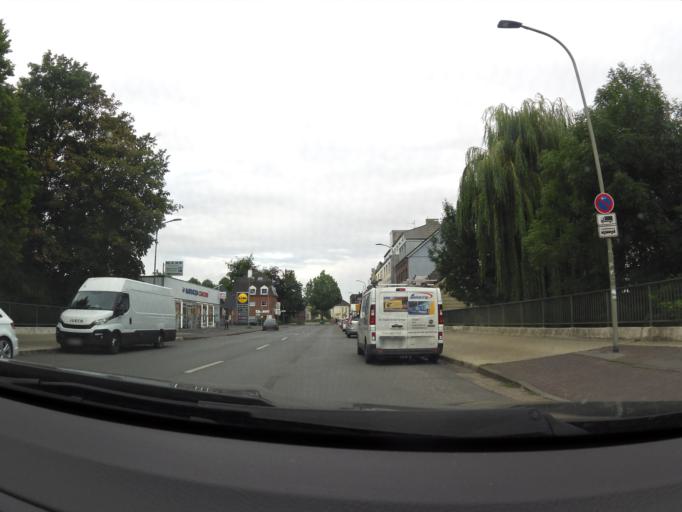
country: DE
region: North Rhine-Westphalia
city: Geldern
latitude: 51.5200
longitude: 6.3164
